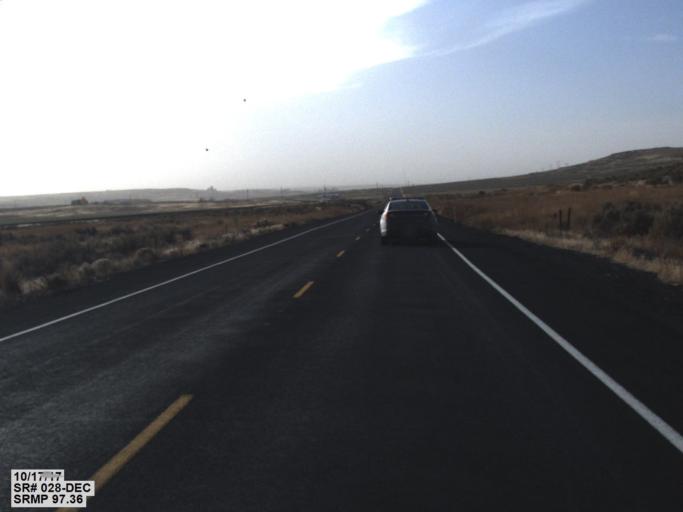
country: US
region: Washington
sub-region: Adams County
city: Ritzville
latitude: 47.3399
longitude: -118.6202
